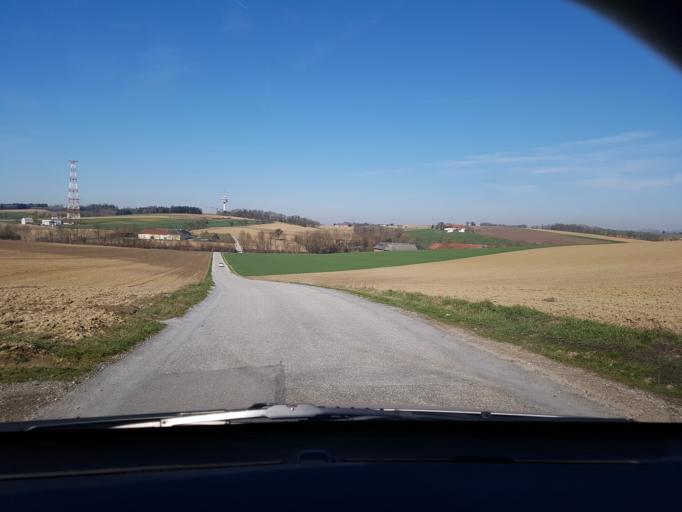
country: AT
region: Upper Austria
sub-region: Politischer Bezirk Linz-Land
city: Ansfelden
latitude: 48.1953
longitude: 14.3192
